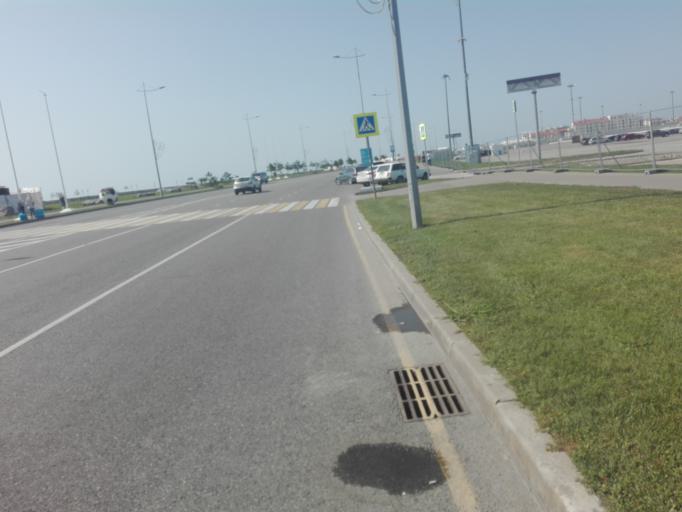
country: RU
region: Krasnodarskiy
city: Adler
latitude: 43.4000
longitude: 39.9511
